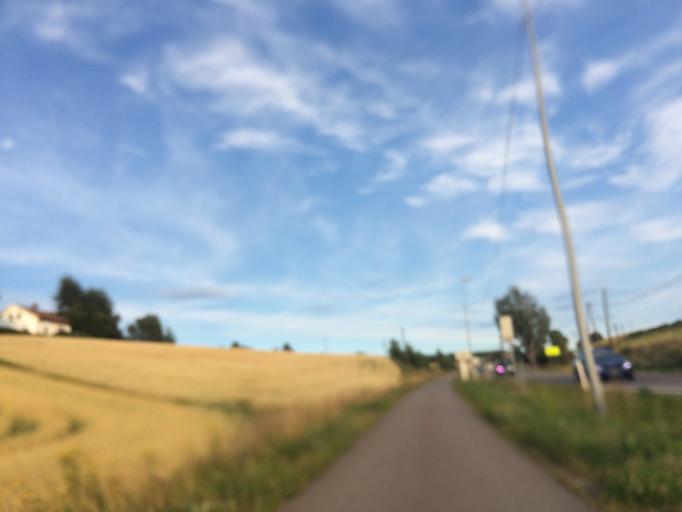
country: NO
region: Akershus
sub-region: Ski
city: Ski
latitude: 59.6722
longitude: 10.8905
